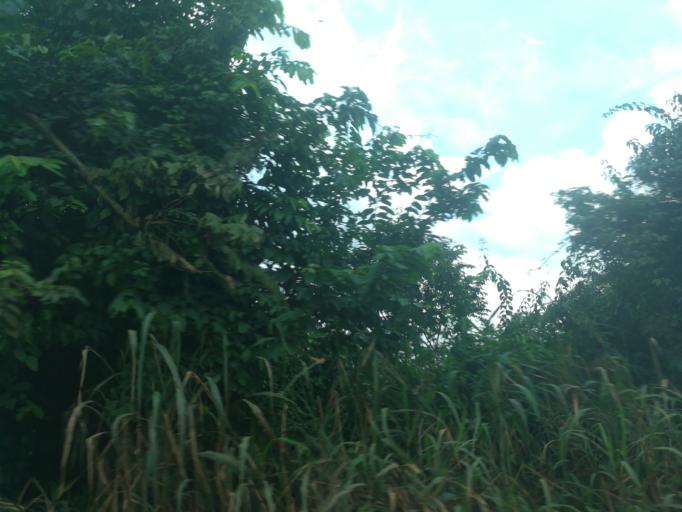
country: NG
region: Lagos
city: Ikorodu
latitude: 6.6700
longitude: 3.6440
